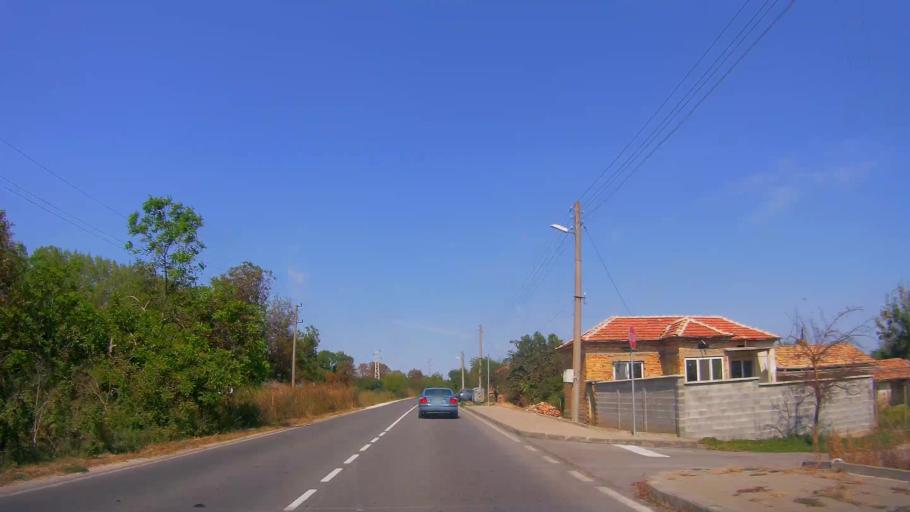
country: BG
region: Shumen
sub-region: Obshtina Smyadovo
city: Smyadovo
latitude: 43.1802
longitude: 27.0067
